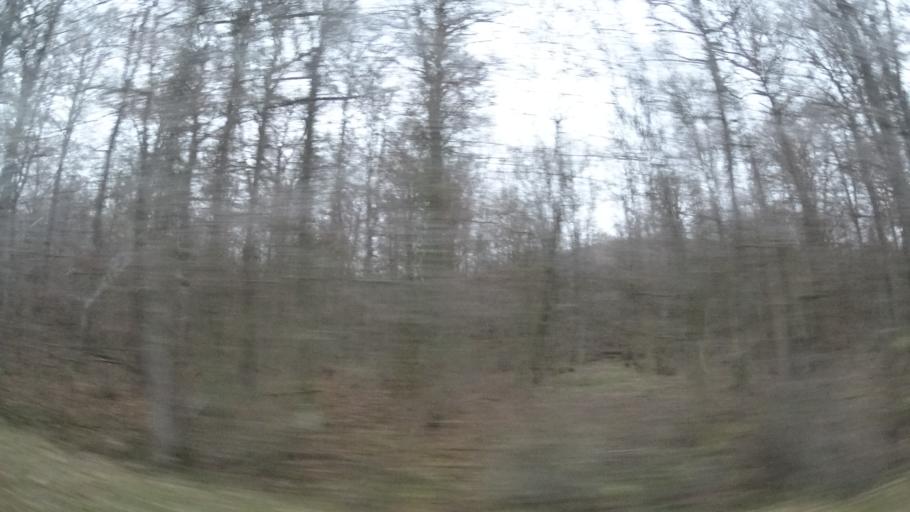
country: DE
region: Hesse
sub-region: Regierungsbezirk Kassel
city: Rasdorf
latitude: 50.7124
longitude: 9.8605
